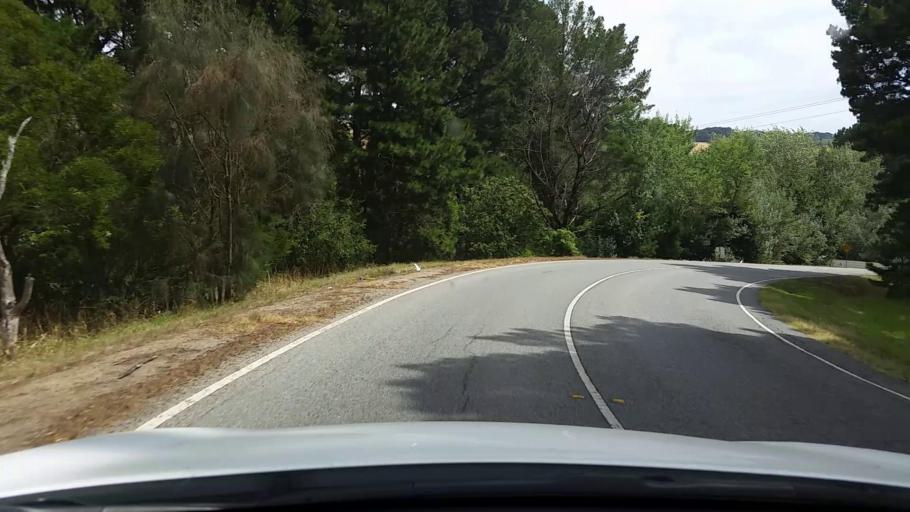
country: AU
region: Victoria
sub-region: Mornington Peninsula
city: Rosebud
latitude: -38.4793
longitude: 144.9482
